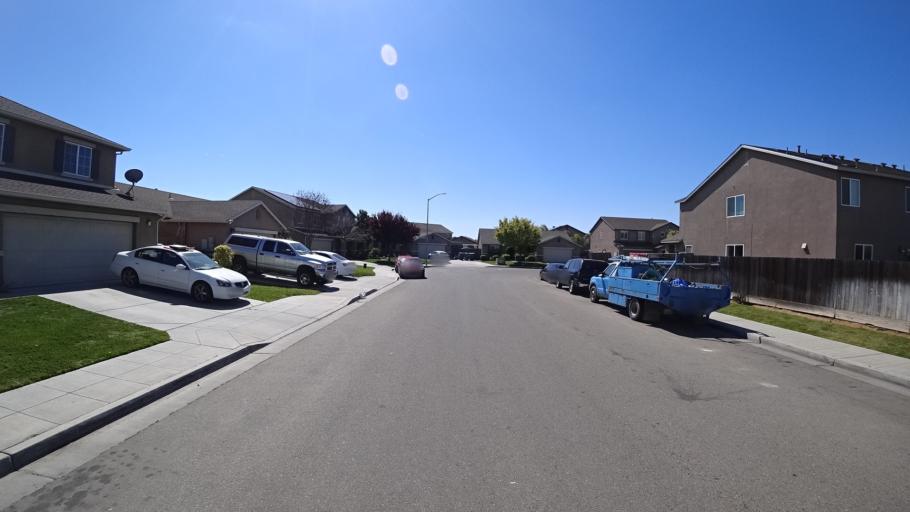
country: US
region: California
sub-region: Fresno County
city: West Park
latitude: 36.7854
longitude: -119.8943
